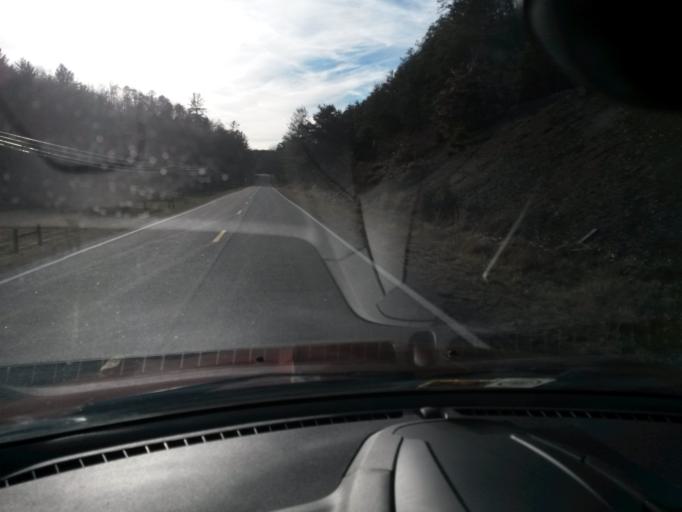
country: US
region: Virginia
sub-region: Alleghany County
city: Clifton Forge
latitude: 37.8423
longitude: -79.7541
